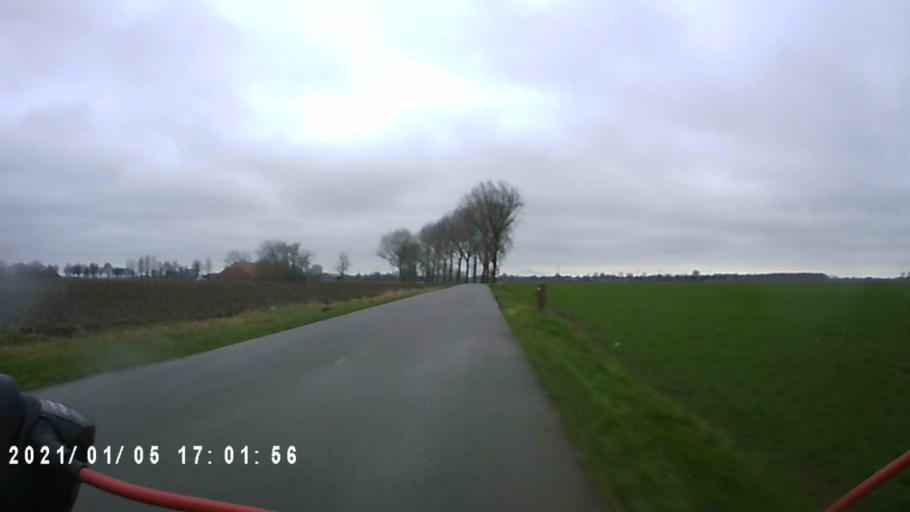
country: NL
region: Groningen
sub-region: Gemeente  Oldambt
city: Winschoten
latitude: 53.2580
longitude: 7.0433
